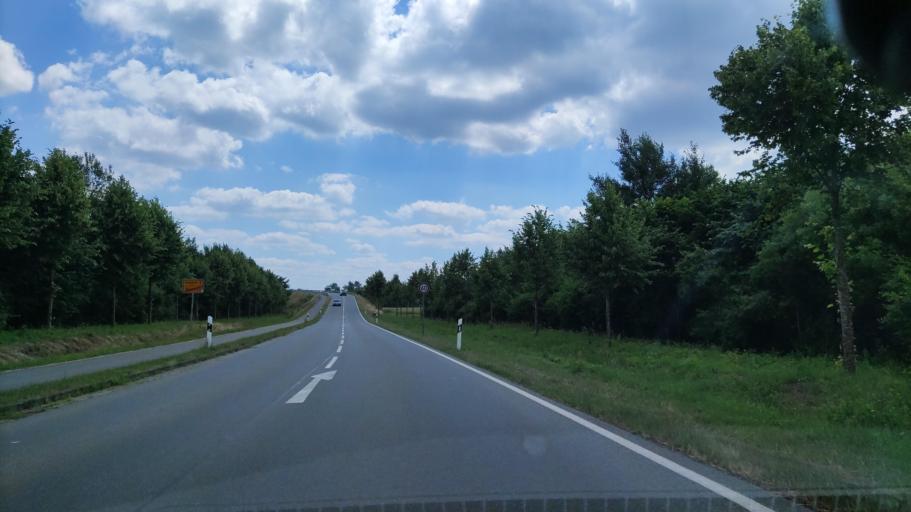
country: DE
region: Mecklenburg-Vorpommern
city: Hagenow
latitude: 53.3755
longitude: 11.1450
